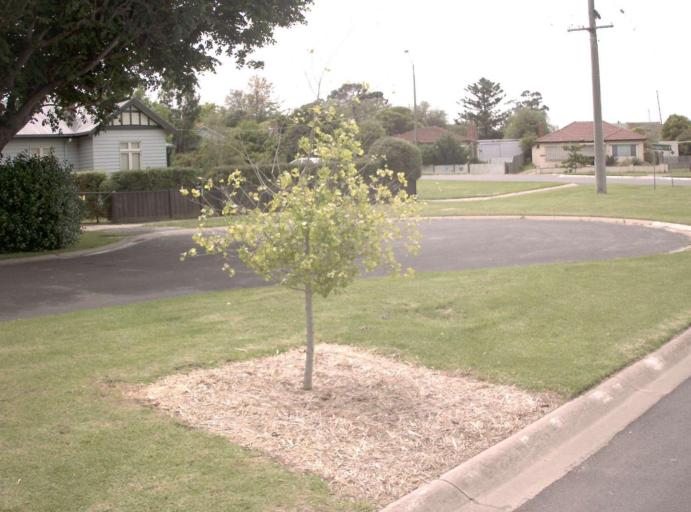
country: AU
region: Victoria
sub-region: Wellington
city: Sale
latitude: -37.9710
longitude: 146.9834
